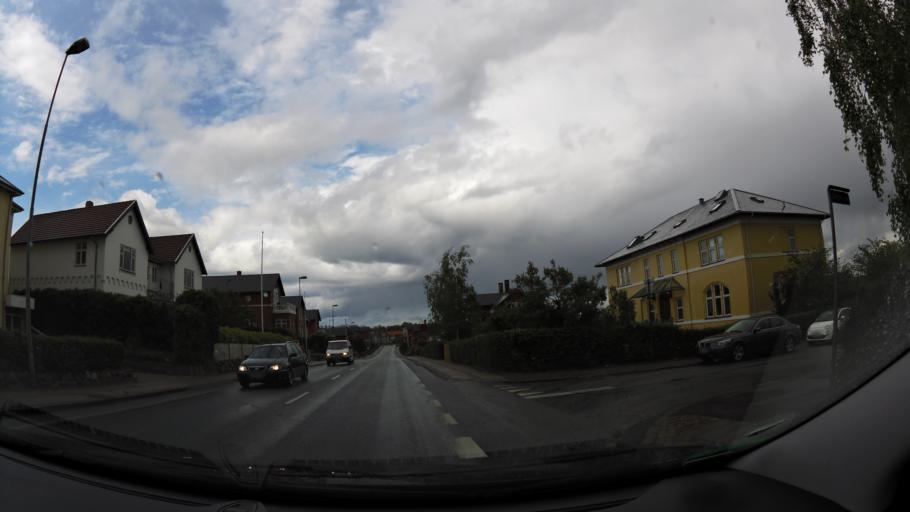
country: DK
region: South Denmark
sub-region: Nyborg Kommune
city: Nyborg
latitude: 55.3061
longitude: 10.7843
